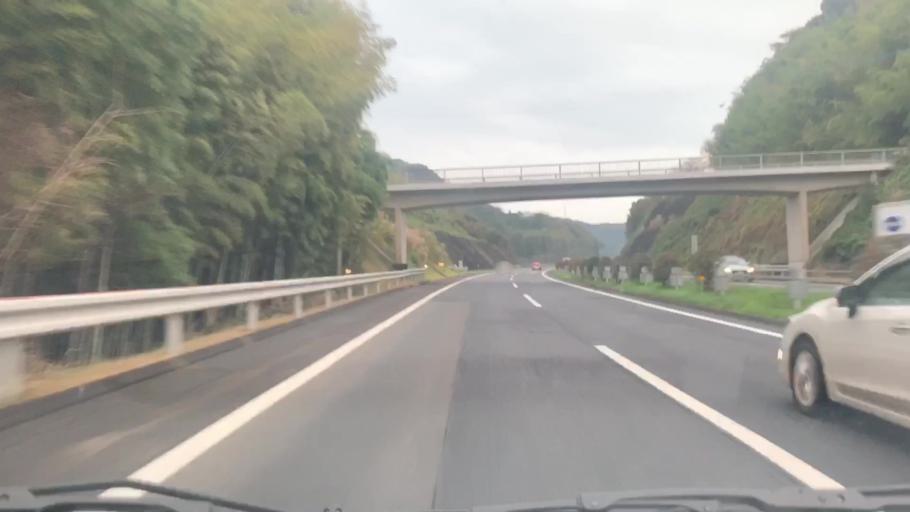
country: JP
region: Nagasaki
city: Omura
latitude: 32.8860
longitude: 129.9942
